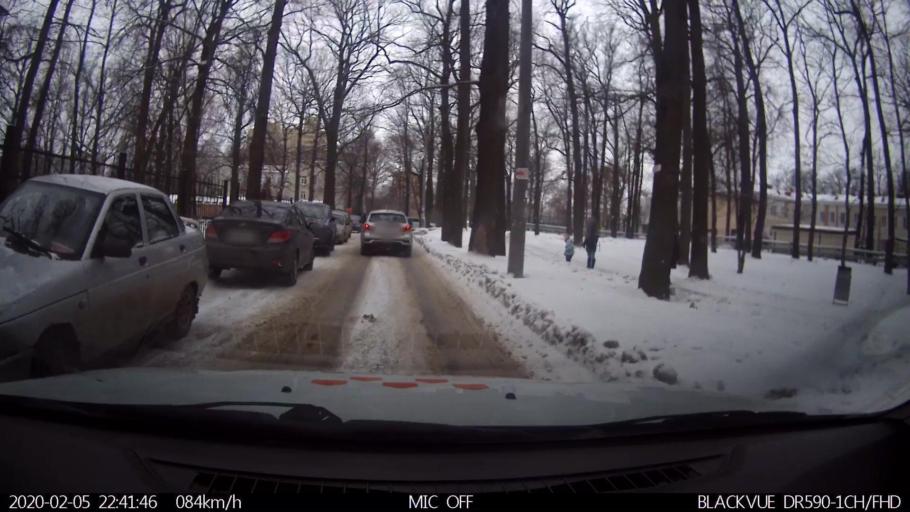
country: RU
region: Nizjnij Novgorod
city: Imeni Stepana Razina
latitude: 54.7200
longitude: 44.3444
